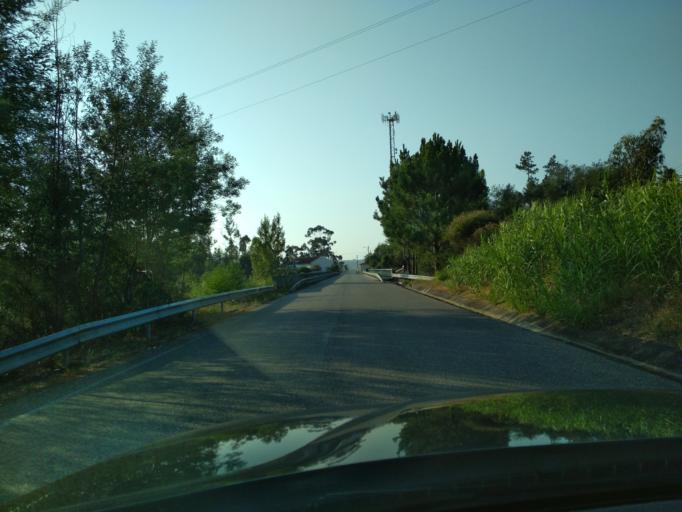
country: PT
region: Aveiro
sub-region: Mealhada
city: Pampilhosa do Botao
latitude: 40.2695
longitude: -8.4550
